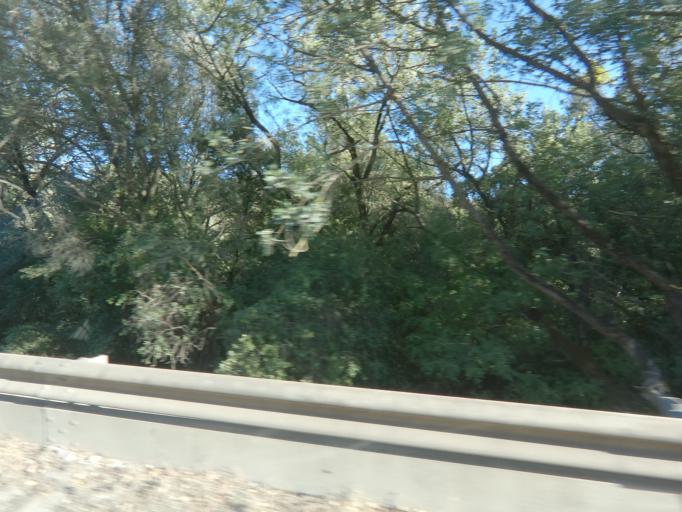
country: PT
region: Setubal
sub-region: Setubal
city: Setubal
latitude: 38.5034
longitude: -8.9428
